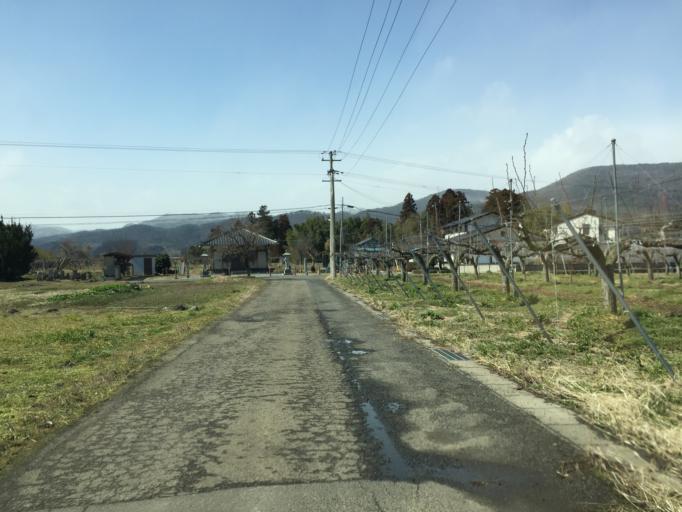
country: JP
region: Fukushima
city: Fukushima-shi
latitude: 37.8004
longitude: 140.4211
